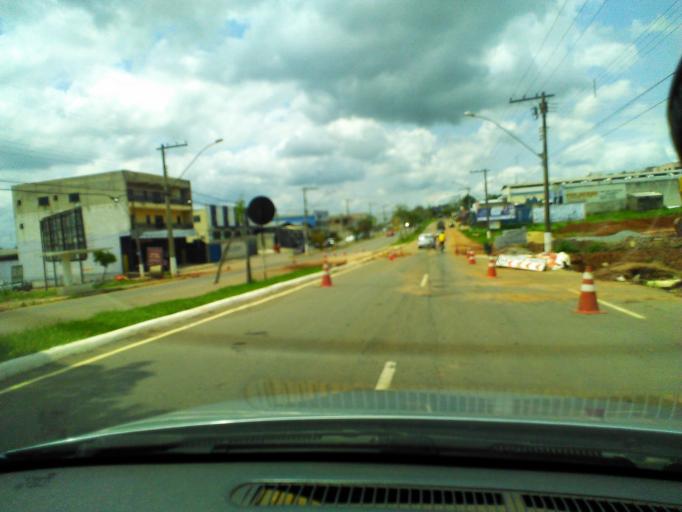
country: BR
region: Minas Gerais
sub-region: Tres Coracoes
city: Tres Coracoes
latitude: -21.6751
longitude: -45.2702
